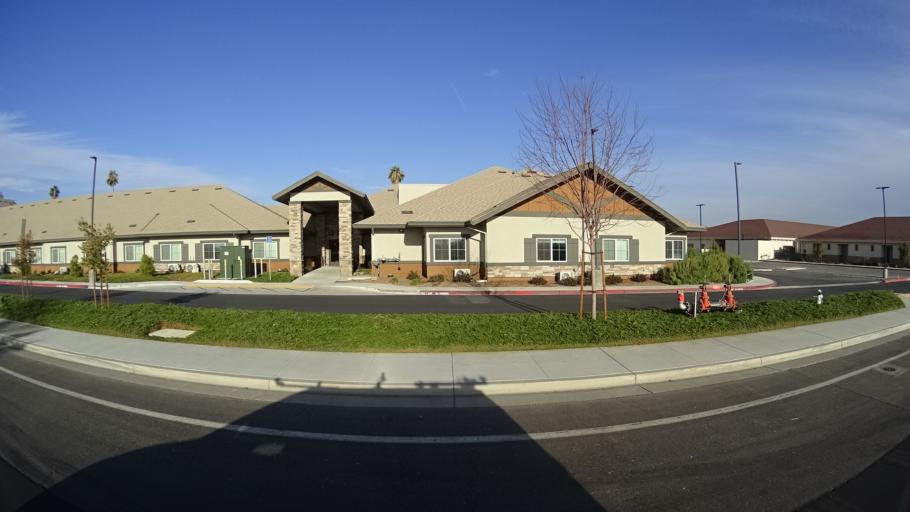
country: US
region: California
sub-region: Kern County
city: Oildale
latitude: 35.4051
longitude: -119.0597
